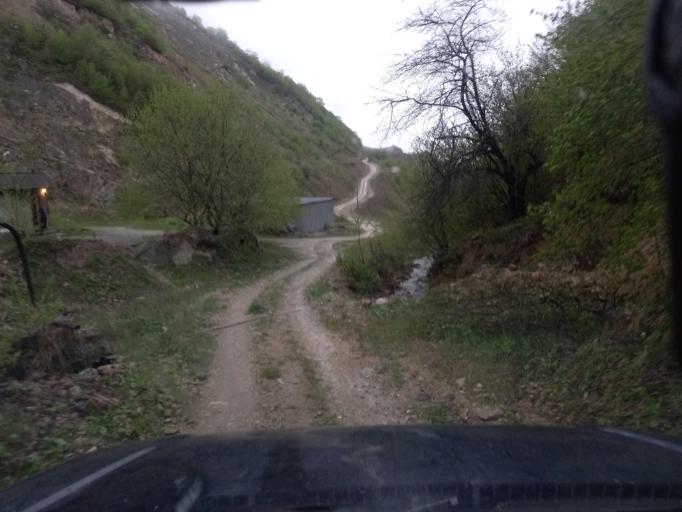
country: RU
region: Kabardino-Balkariya
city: Zhankhoteko
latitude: 43.4973
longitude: 43.1544
